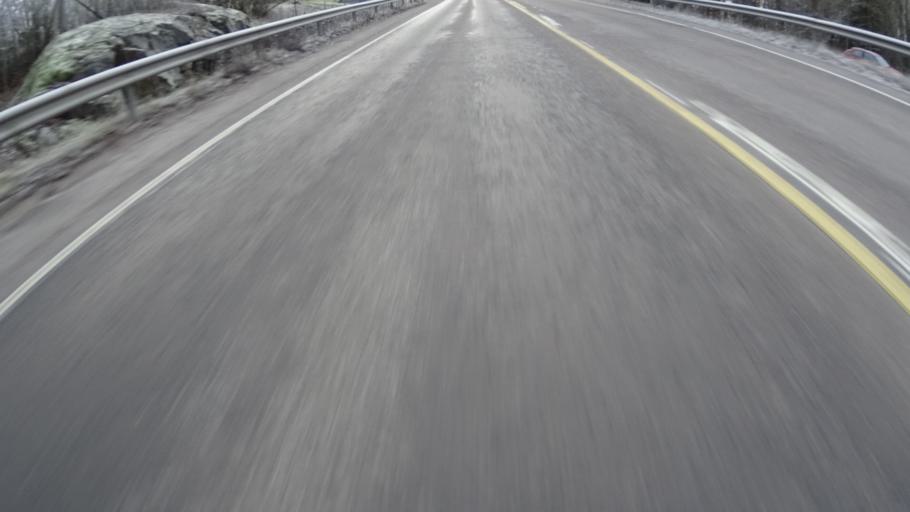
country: FI
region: Uusimaa
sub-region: Helsinki
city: Nurmijaervi
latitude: 60.4052
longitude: 24.7311
